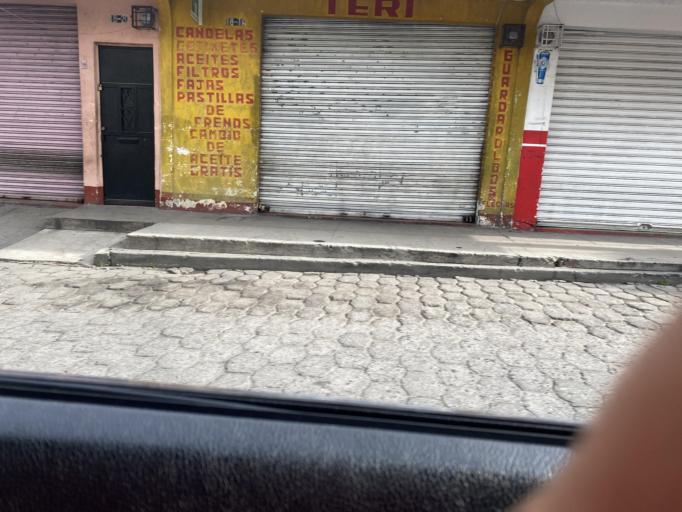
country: GT
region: Quetzaltenango
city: Quetzaltenango
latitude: 14.8507
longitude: -91.5215
